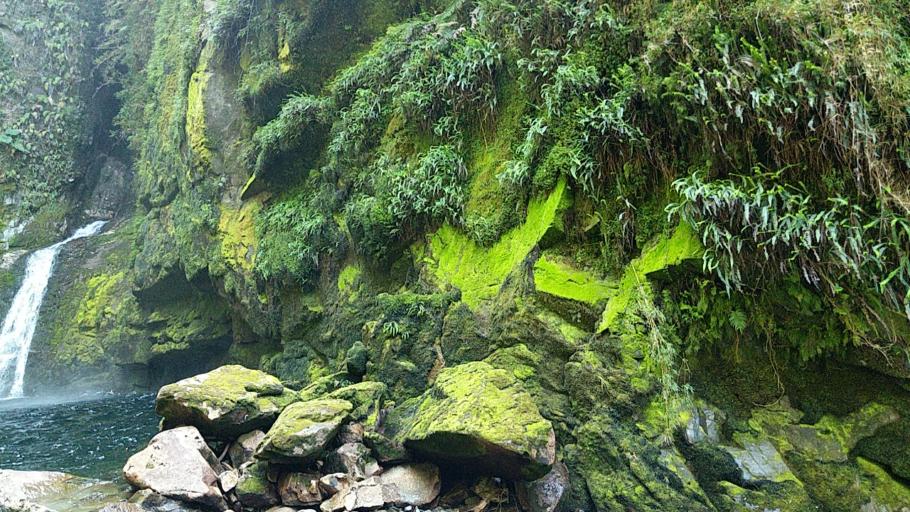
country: CL
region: Los Lagos
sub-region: Provincia de Palena
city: Chaiten
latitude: -42.6770
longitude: -72.5851
